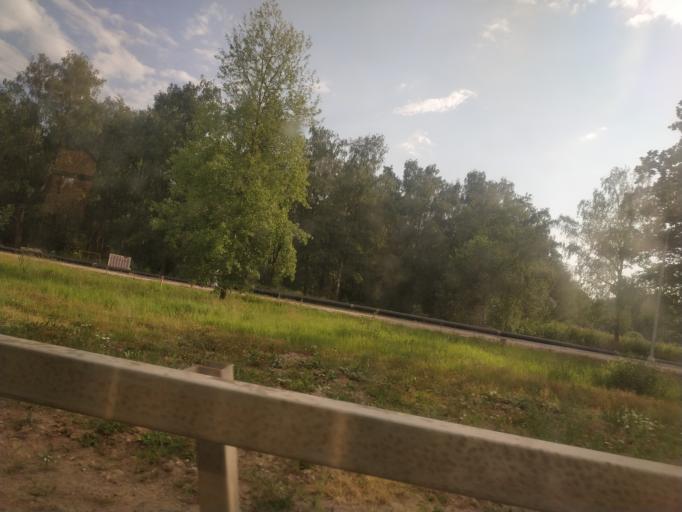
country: RU
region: Moskovskaya
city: Mosrentgen
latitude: 55.5862
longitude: 37.4577
